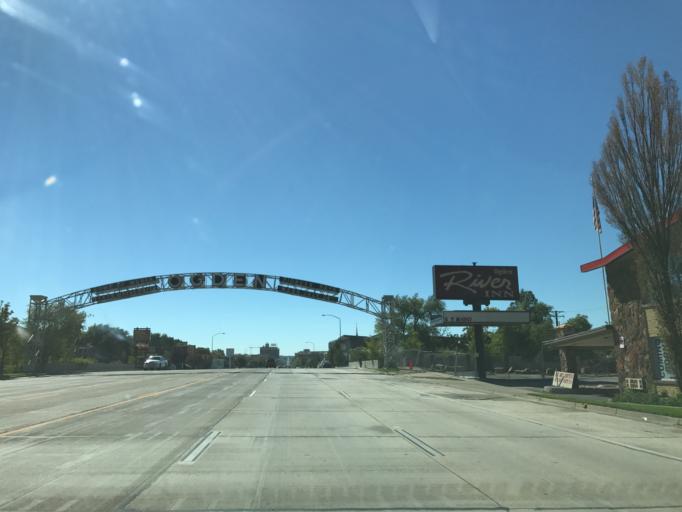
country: US
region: Utah
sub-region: Weber County
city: Ogden
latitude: 41.2344
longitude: -111.9702
